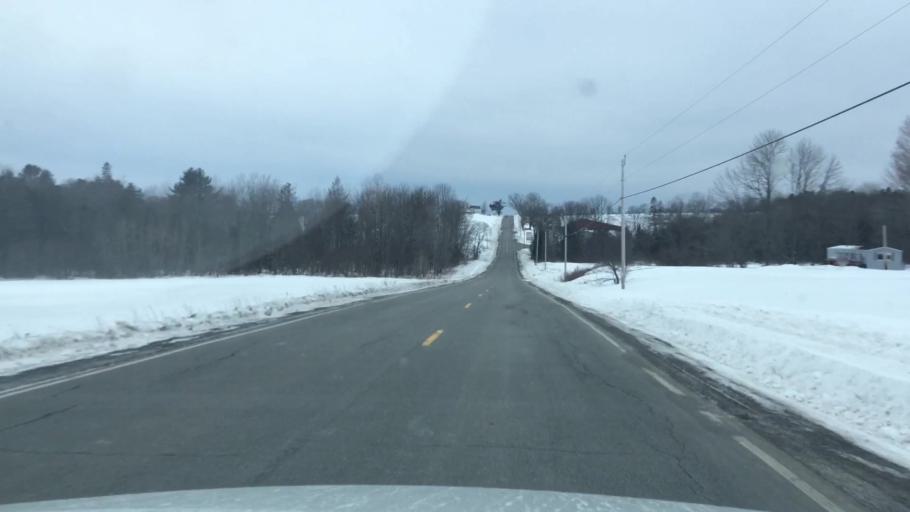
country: US
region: Maine
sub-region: Penobscot County
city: Garland
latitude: 44.9681
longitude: -69.1568
